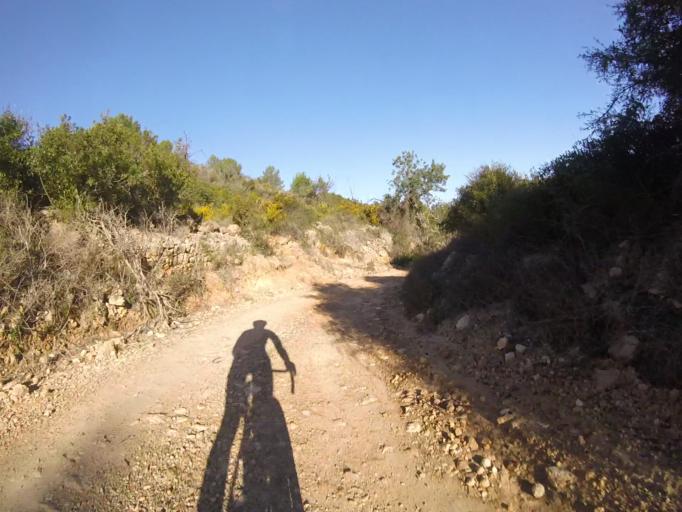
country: ES
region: Valencia
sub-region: Provincia de Castello
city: Torreblanca
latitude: 40.2566
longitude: 0.1918
